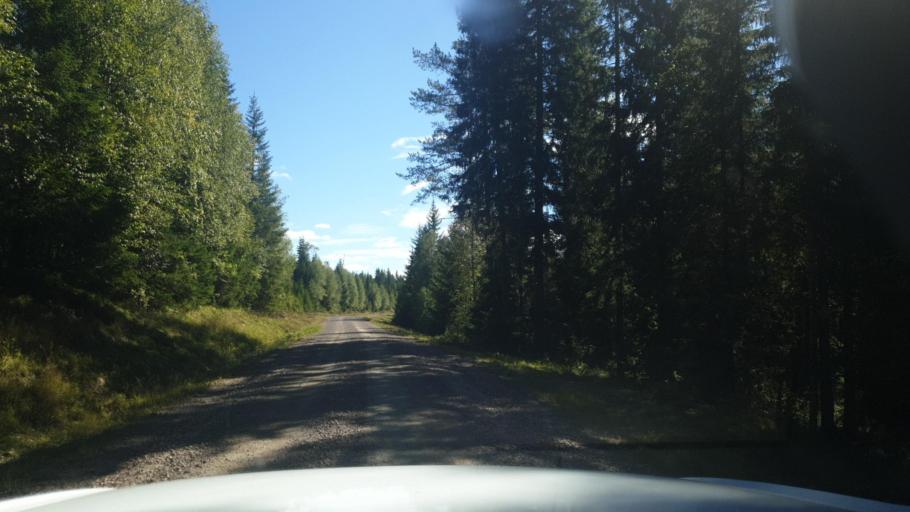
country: SE
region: Vaermland
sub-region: Eda Kommun
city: Charlottenberg
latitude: 60.1269
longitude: 12.5953
